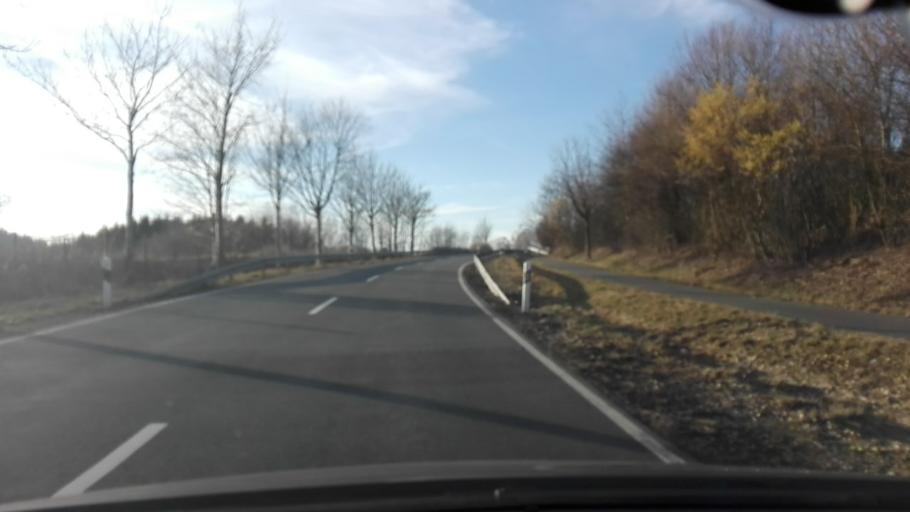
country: DE
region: North Rhine-Westphalia
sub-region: Regierungsbezirk Arnsberg
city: Schmallenberg
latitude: 51.1541
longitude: 8.2713
